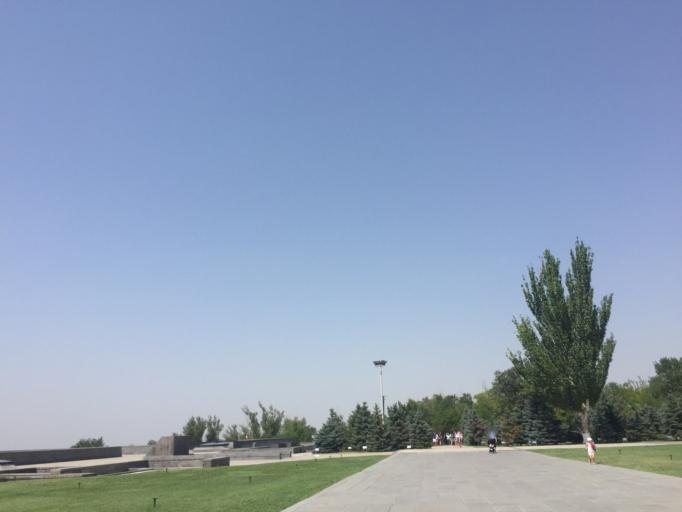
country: AM
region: Yerevan
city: Yerevan
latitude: 40.1858
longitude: 44.4890
